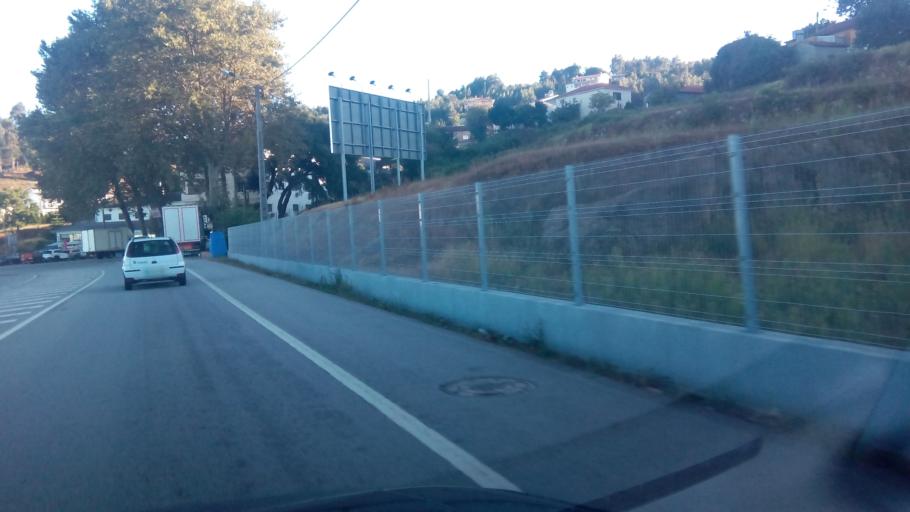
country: PT
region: Porto
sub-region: Paredes
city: Gandra
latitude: 41.1930
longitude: -8.4071
